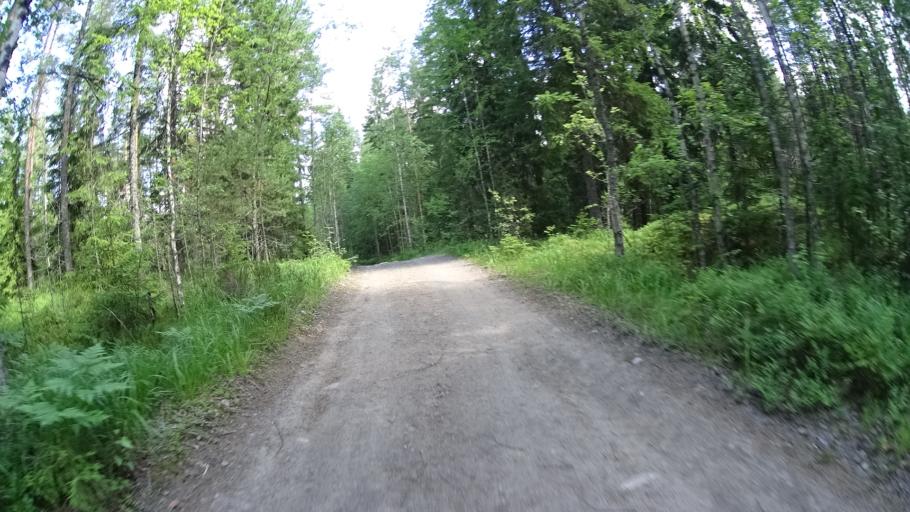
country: FI
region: Uusimaa
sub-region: Helsinki
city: Vihti
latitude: 60.3268
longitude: 24.4603
